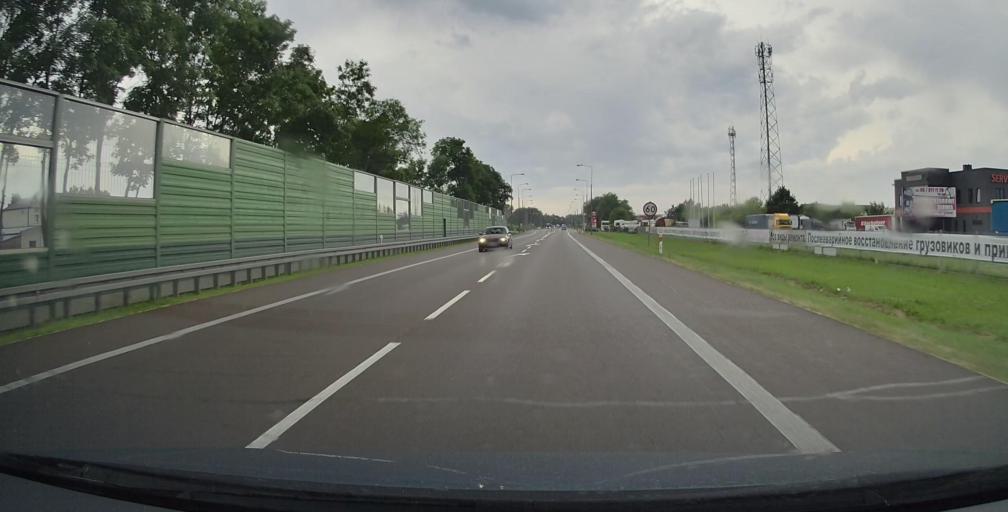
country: PL
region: Lublin Voivodeship
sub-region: Powiat bialski
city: Miedzyrzec Podlaski
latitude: 52.0003
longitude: 22.7707
